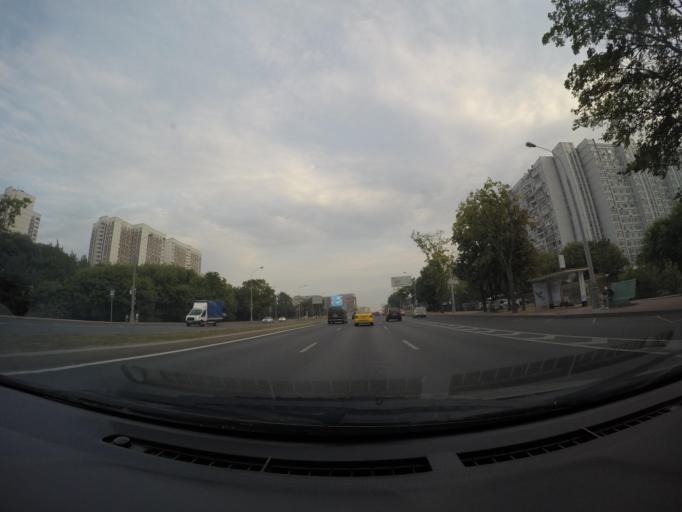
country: RU
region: Moscow
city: Orekhovo-Borisovo
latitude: 55.6268
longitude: 37.7095
